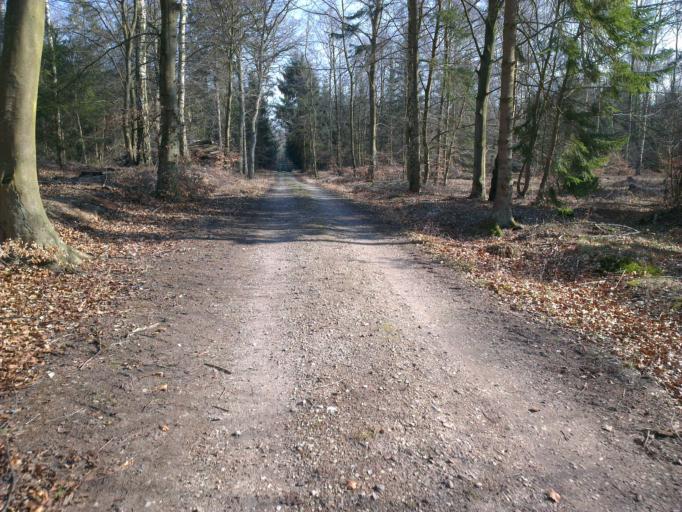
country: DK
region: Capital Region
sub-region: Frederikssund Kommune
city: Jaegerspris
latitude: 55.9044
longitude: 11.9942
